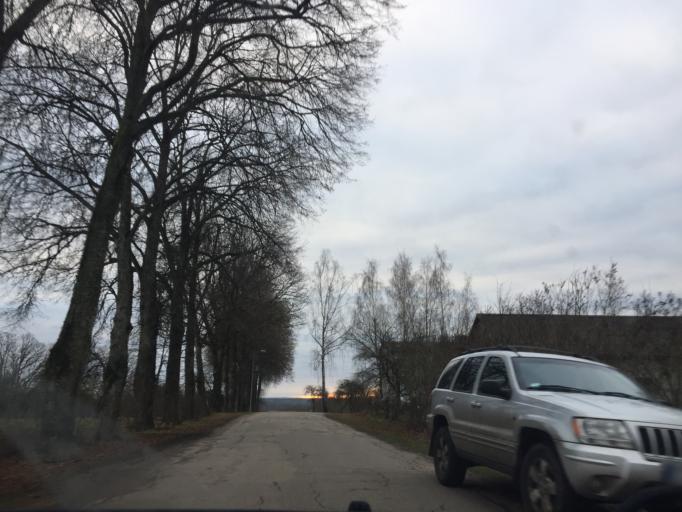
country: LV
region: Krimulda
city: Ragana
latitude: 57.1583
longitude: 24.7020
